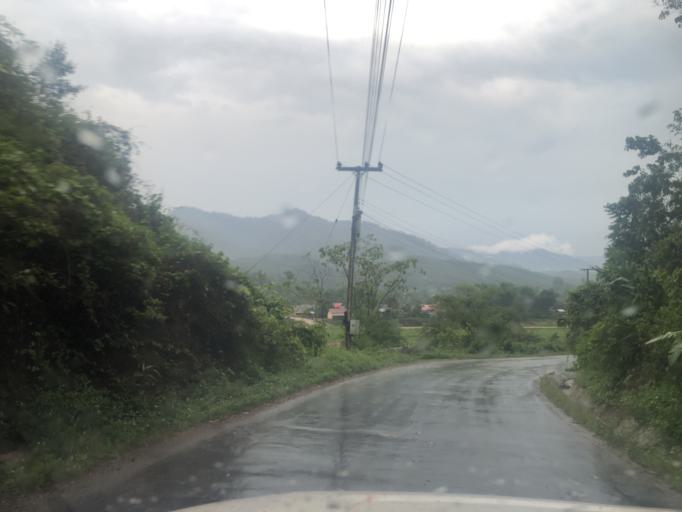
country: LA
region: Phongsali
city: Phongsali
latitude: 21.4059
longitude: 101.9610
